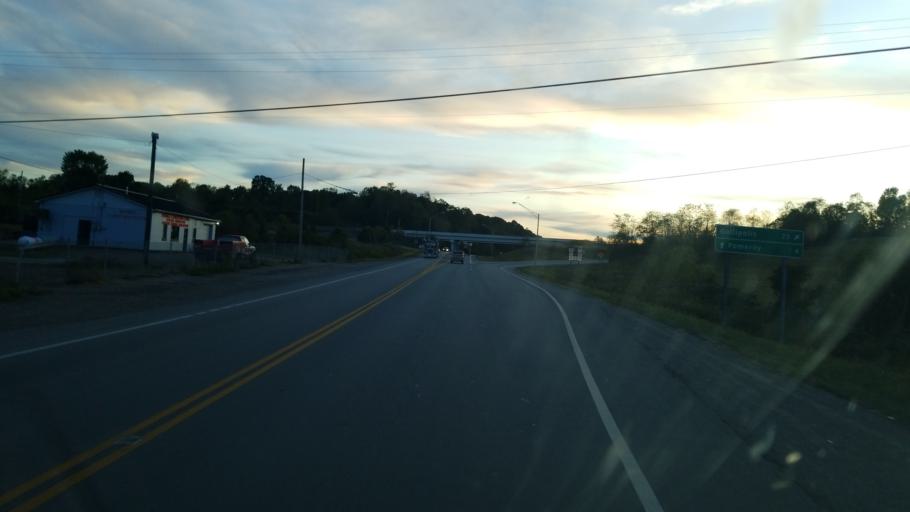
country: US
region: Ohio
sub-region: Meigs County
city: Pomeroy
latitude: 39.0551
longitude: -81.9714
